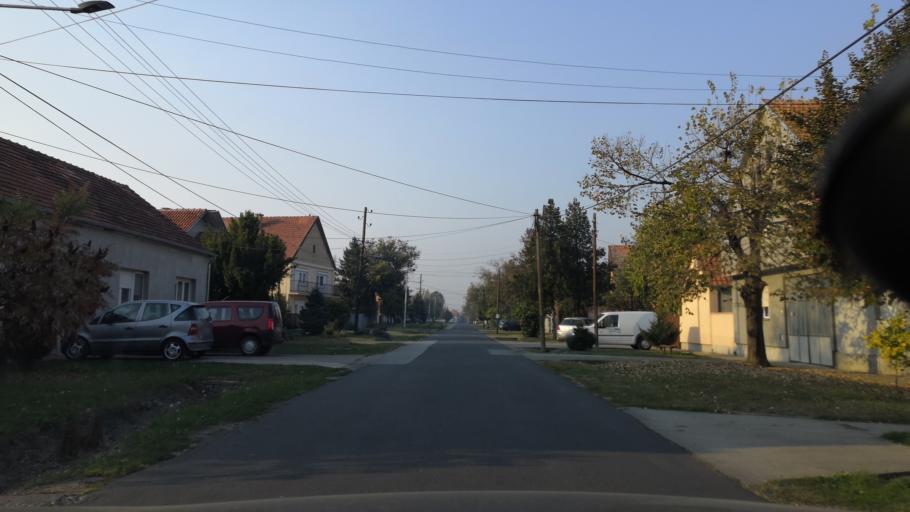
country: RS
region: Autonomna Pokrajina Vojvodina
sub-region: Sremski Okrug
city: Stara Pazova
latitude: 44.9916
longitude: 20.1482
